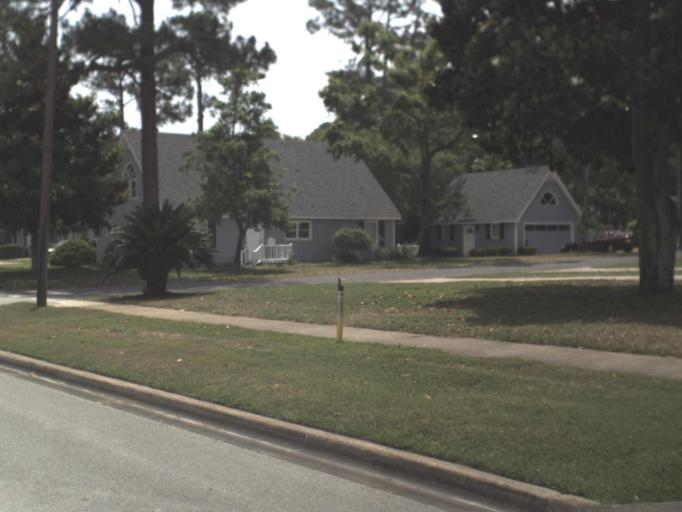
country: US
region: Florida
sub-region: Nassau County
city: Fernandina Beach
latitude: 30.6694
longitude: -81.4469
